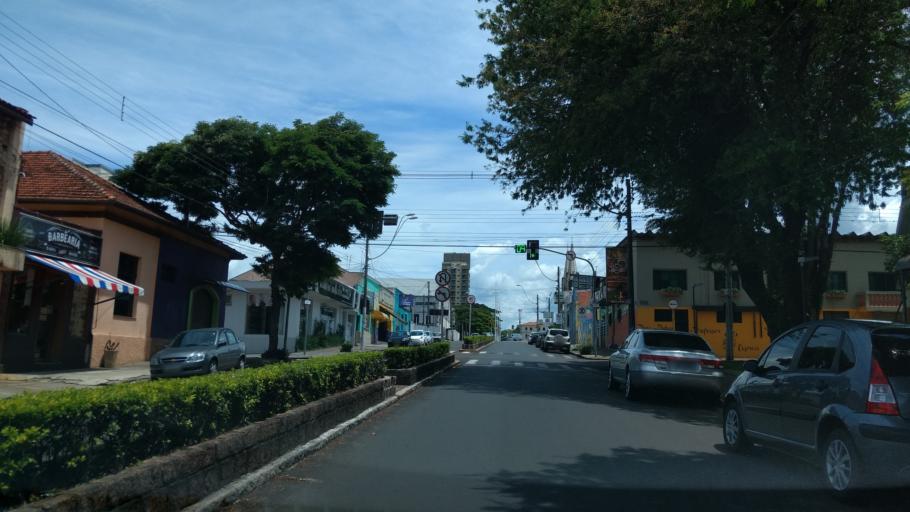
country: BR
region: Sao Paulo
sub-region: Botucatu
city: Botucatu
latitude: -22.8831
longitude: -48.4442
